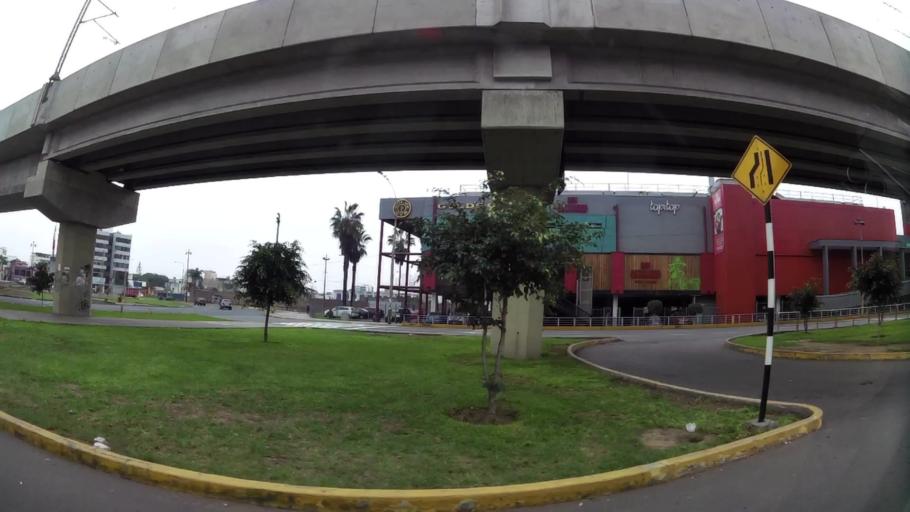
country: PE
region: Lima
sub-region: Lima
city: Surco
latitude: -12.1280
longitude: -77.0006
